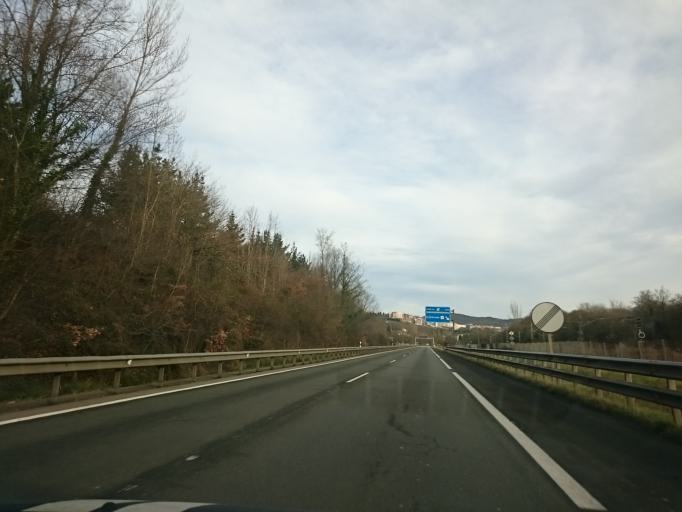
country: ES
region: Asturias
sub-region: Province of Asturias
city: Oviedo
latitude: 43.3335
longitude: -5.8700
